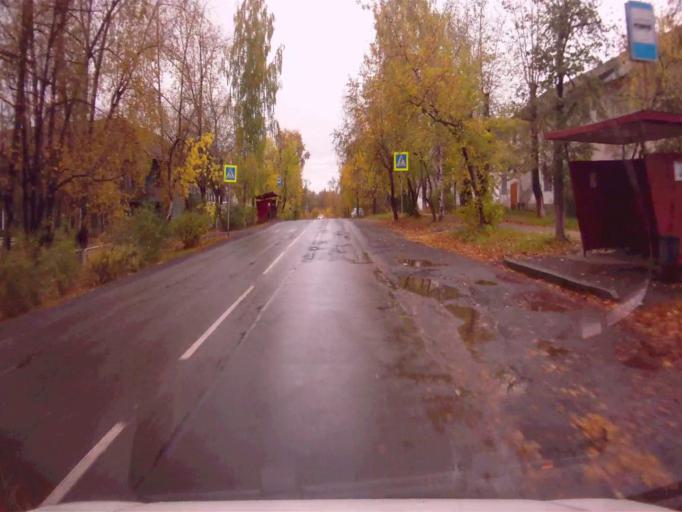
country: RU
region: Chelyabinsk
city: Verkhniy Ufaley
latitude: 56.0404
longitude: 60.2524
